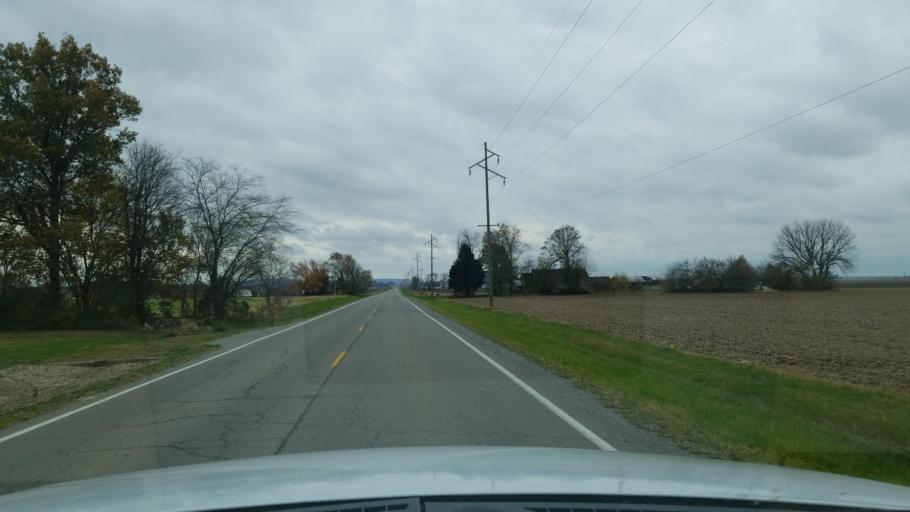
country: US
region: Illinois
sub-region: Saline County
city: Eldorado
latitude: 37.7894
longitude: -88.4382
